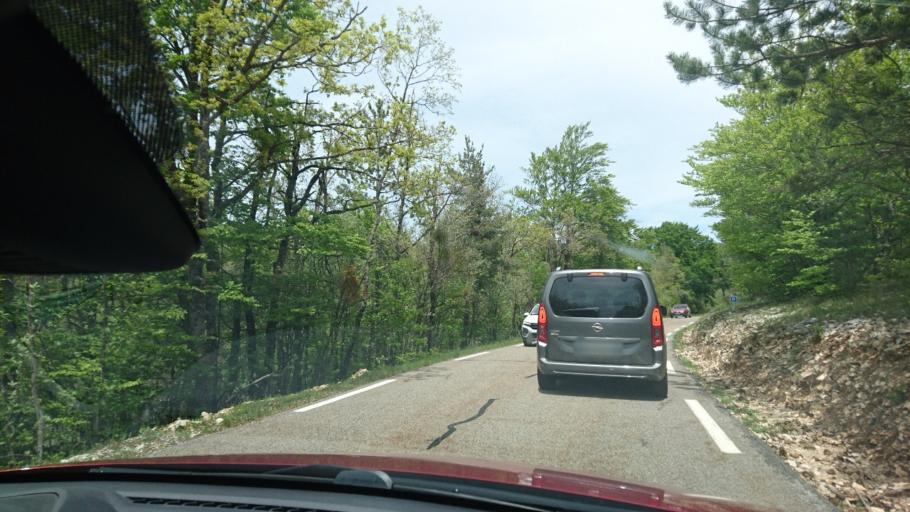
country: FR
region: Provence-Alpes-Cote d'Azur
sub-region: Departement du Vaucluse
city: Sault
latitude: 44.1410
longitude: 5.3685
